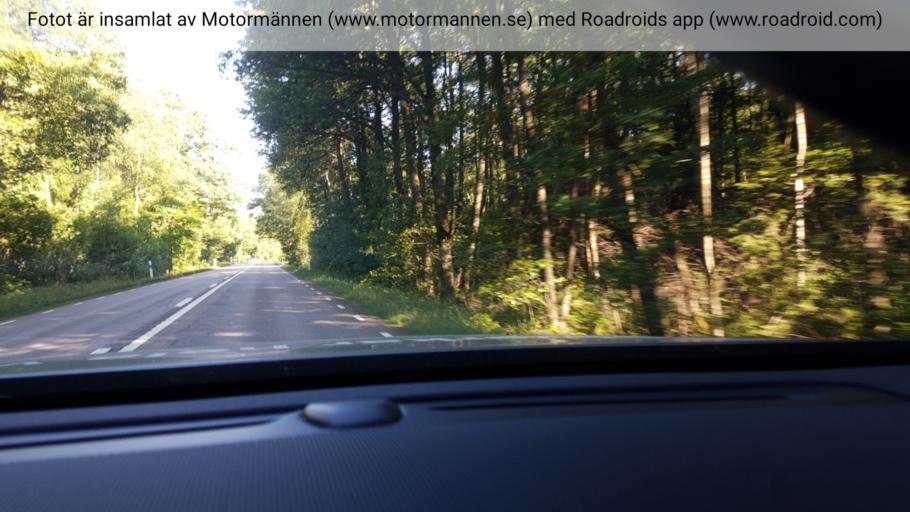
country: SE
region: Kronoberg
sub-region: Markaryds Kommun
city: Markaryd
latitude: 56.4141
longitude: 13.6327
